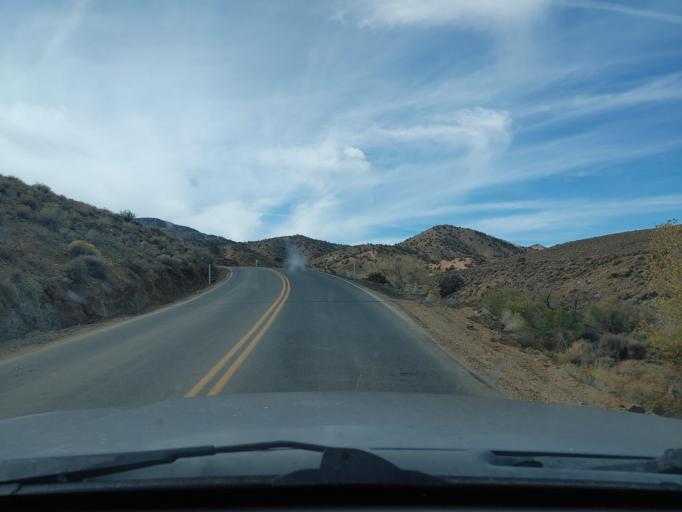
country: US
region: Nevada
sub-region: Lyon County
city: Dayton
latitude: 39.3057
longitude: -119.5640
